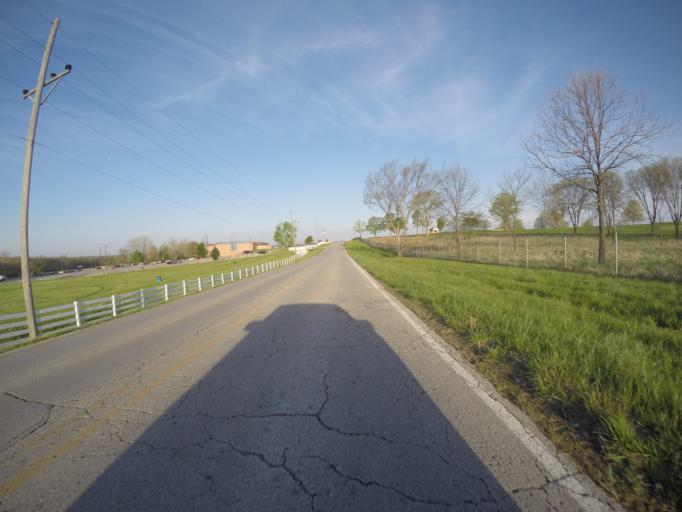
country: US
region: Missouri
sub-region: Jackson County
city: Lees Summit
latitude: 38.9133
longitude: -94.4540
